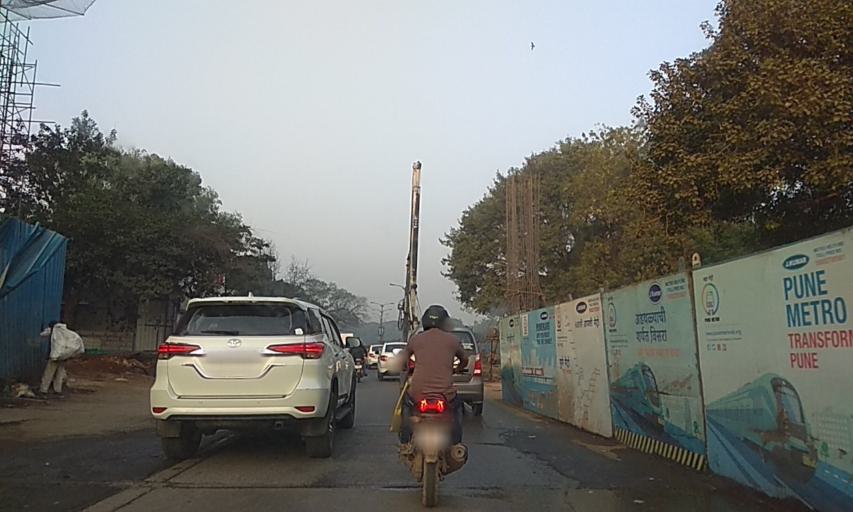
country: IN
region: Maharashtra
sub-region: Pune Division
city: Shivaji Nagar
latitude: 18.5297
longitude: 73.8627
